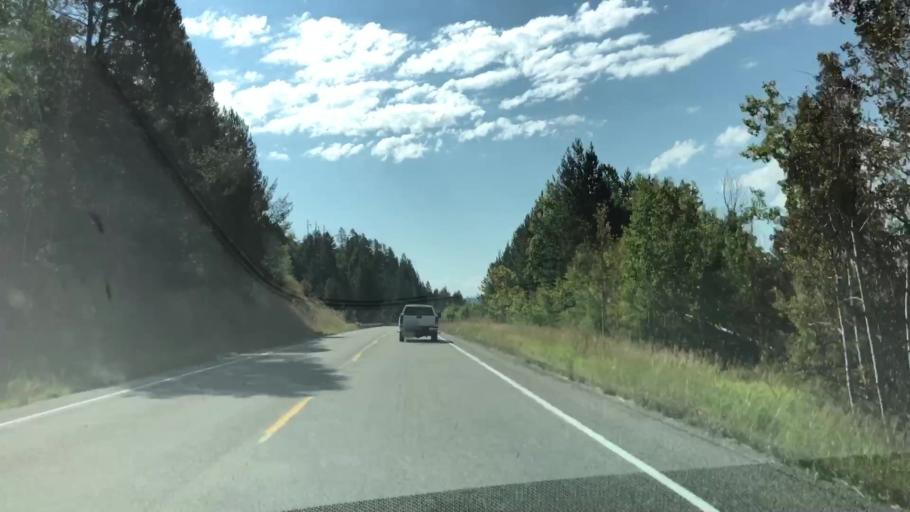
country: US
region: Idaho
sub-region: Teton County
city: Victor
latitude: 43.2907
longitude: -111.1234
